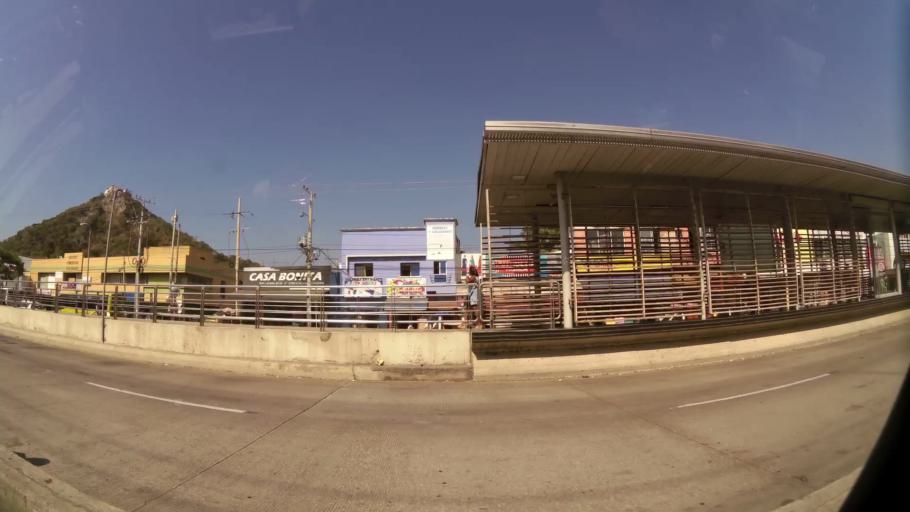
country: CO
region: Bolivar
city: Cartagena
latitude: 10.4138
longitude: -75.5243
